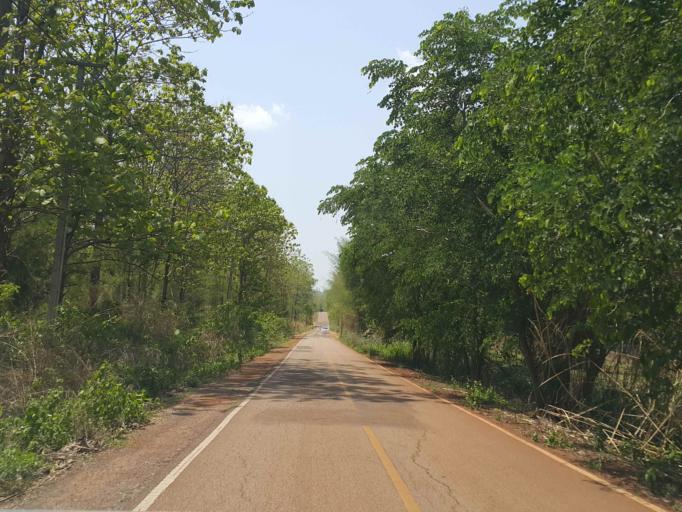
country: TH
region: Chiang Mai
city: Mae Taeng
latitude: 19.0842
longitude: 99.0871
